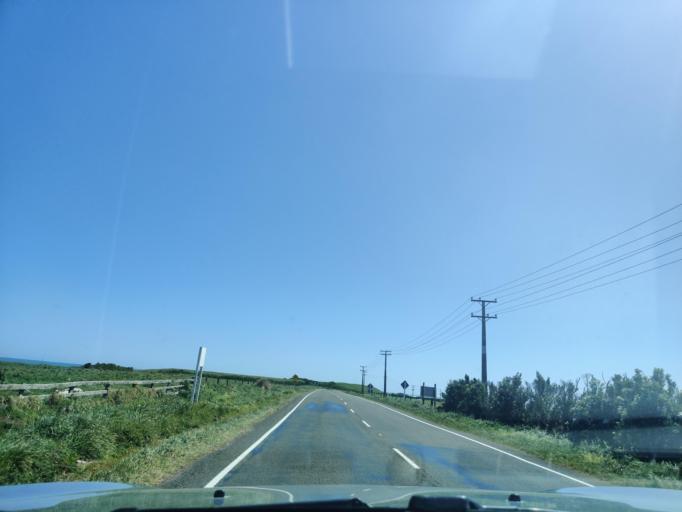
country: NZ
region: Taranaki
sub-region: South Taranaki District
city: Opunake
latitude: -39.4444
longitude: 173.8411
